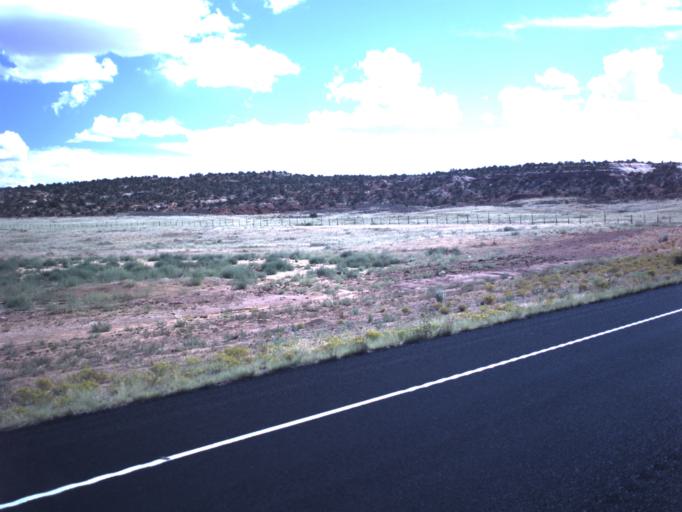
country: US
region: Utah
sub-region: Grand County
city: Moab
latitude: 38.6168
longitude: -109.8141
